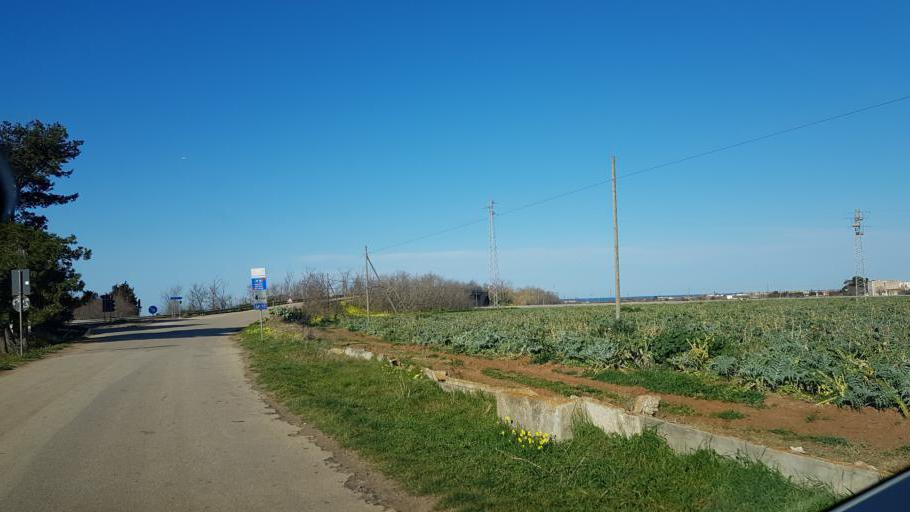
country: IT
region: Apulia
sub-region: Provincia di Brindisi
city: San Vito dei Normanni
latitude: 40.6874
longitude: 17.8226
